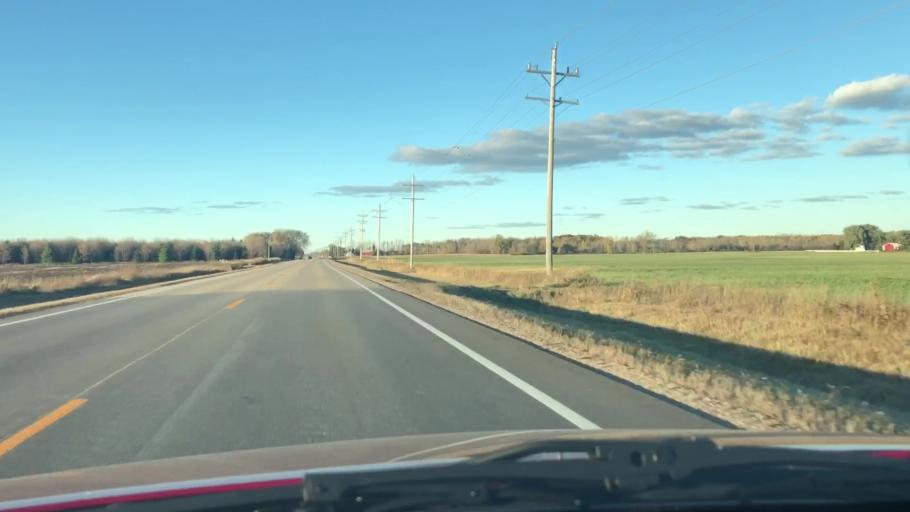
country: US
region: Wisconsin
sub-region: Outagamie County
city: Seymour
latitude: 44.4671
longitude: -88.2913
